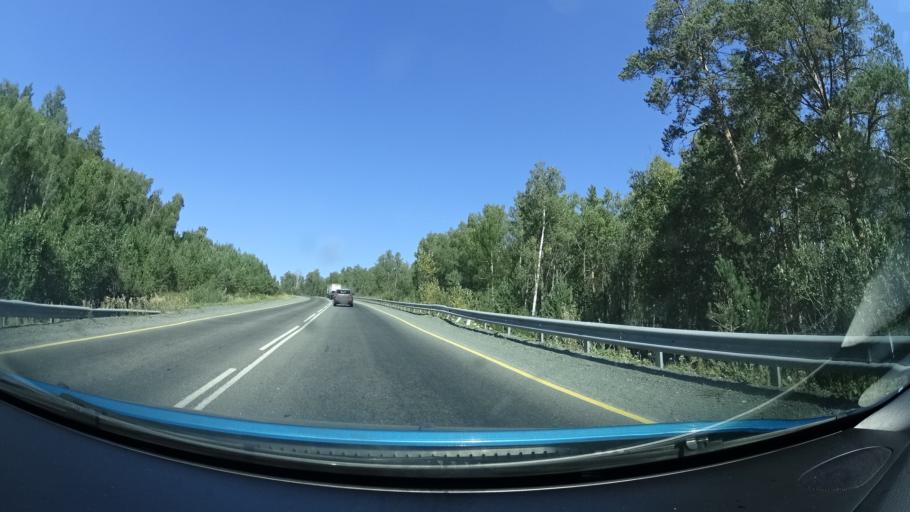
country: RU
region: Bashkortostan
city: Abzakovo
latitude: 53.8885
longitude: 58.5249
